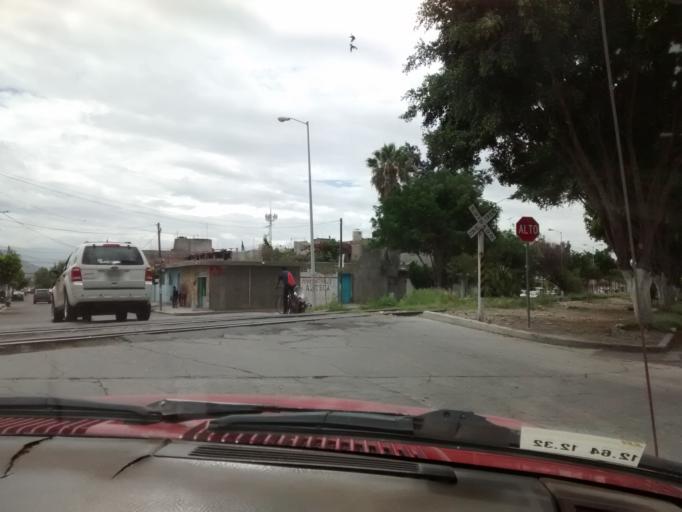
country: MX
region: Puebla
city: Tehuacan
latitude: 18.4676
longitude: -97.4032
